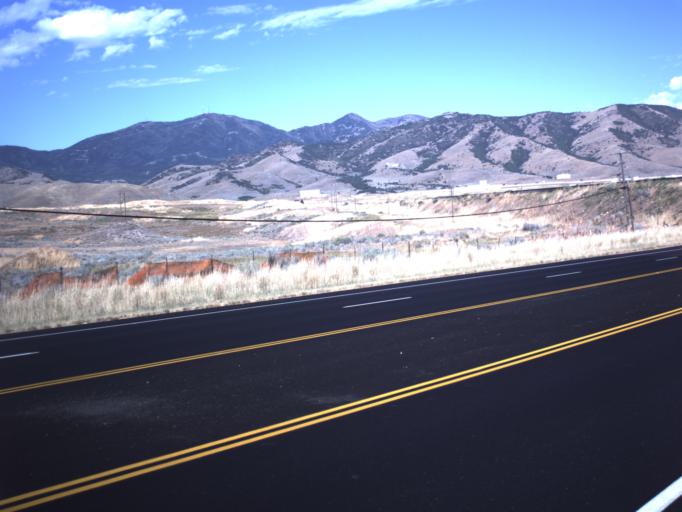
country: US
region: Utah
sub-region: Salt Lake County
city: Oquirrh
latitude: 40.6511
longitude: -112.0728
